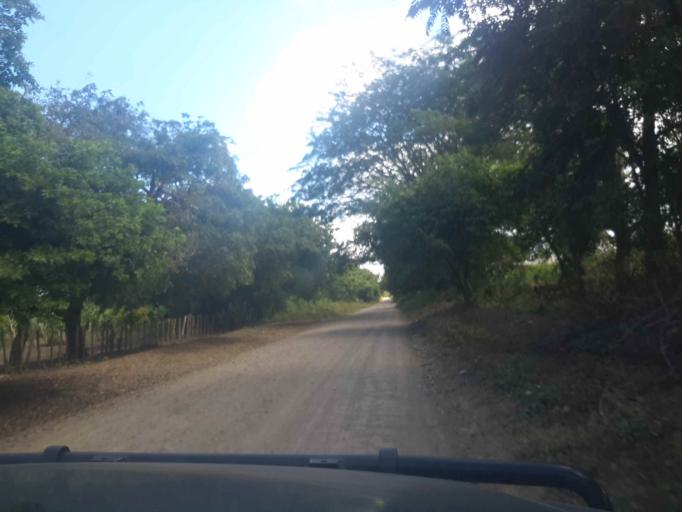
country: NI
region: Granada
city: Nandaime
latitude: 11.6600
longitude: -85.9618
